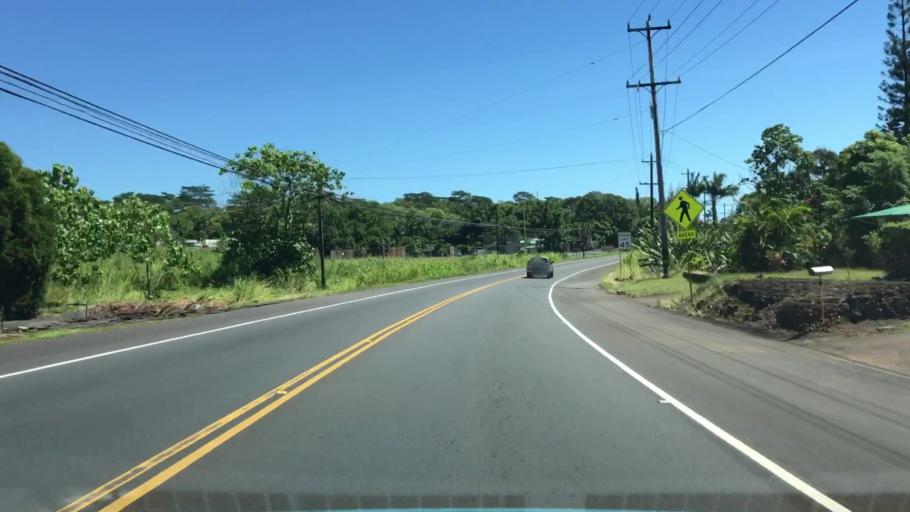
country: US
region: Hawaii
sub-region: Hawaii County
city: Kurtistown
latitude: 19.5900
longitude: -155.0606
